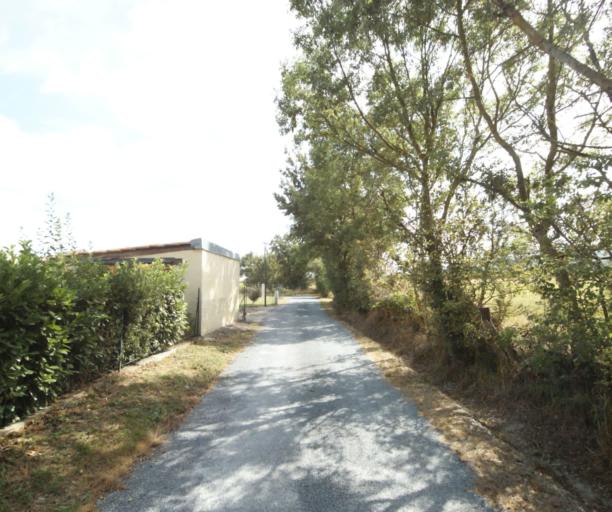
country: FR
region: Midi-Pyrenees
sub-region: Departement du Tarn
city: Soreze
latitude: 43.4726
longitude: 2.0863
